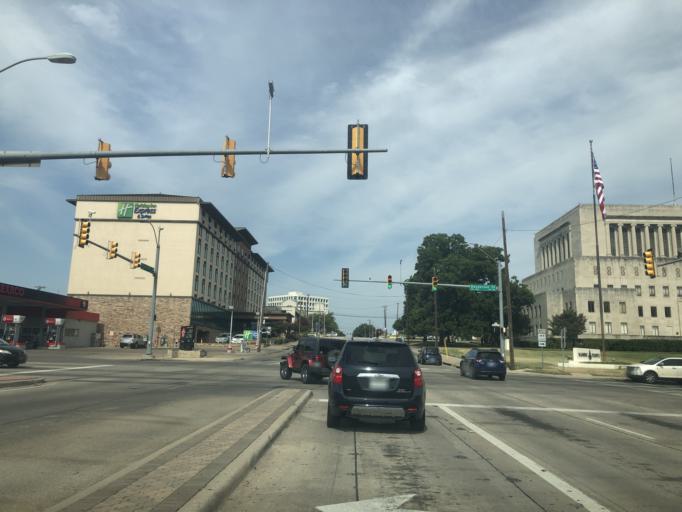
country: US
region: Texas
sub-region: Tarrant County
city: Fort Worth
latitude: 32.7468
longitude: -97.3371
